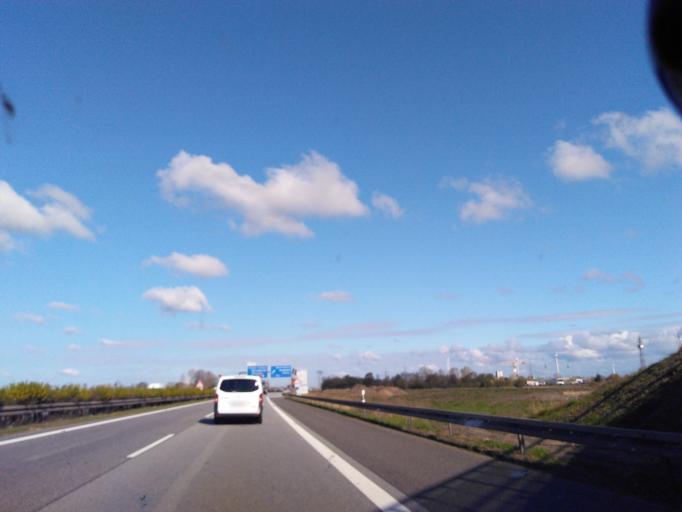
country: DE
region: Berlin
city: Buchholz
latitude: 52.6437
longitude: 13.4262
